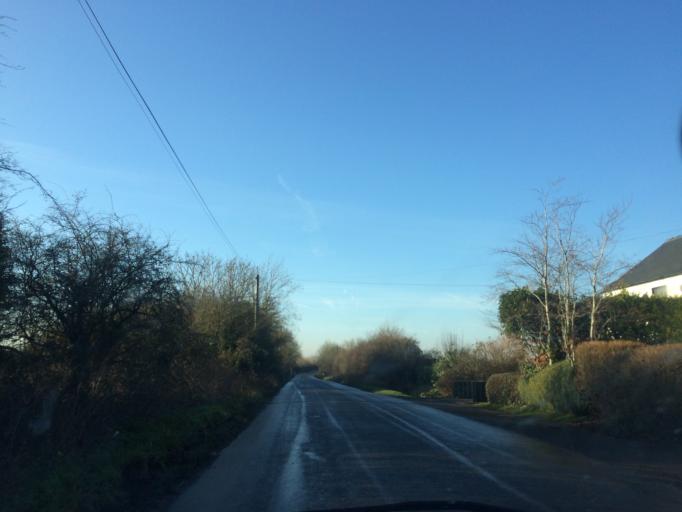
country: GB
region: England
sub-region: Wiltshire
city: Leigh
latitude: 51.6351
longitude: -1.8904
